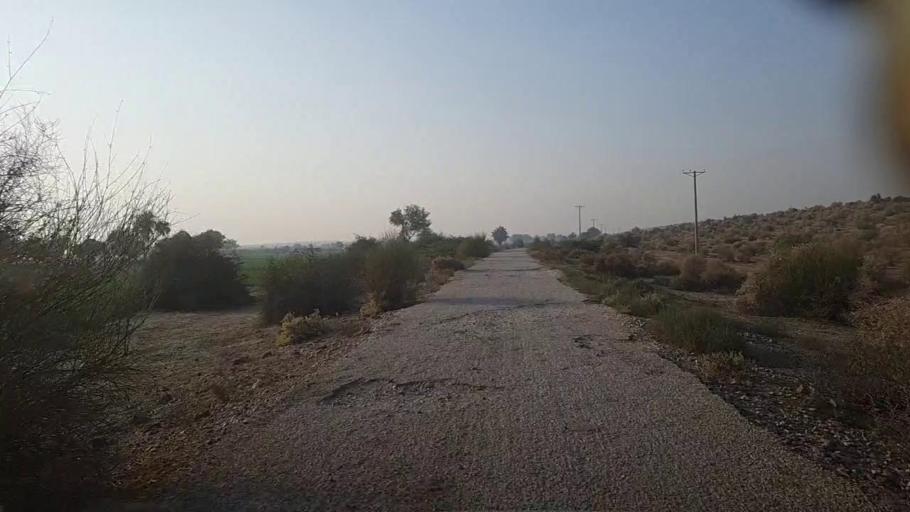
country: PK
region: Sindh
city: Pad Idan
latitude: 26.7154
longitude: 68.4646
